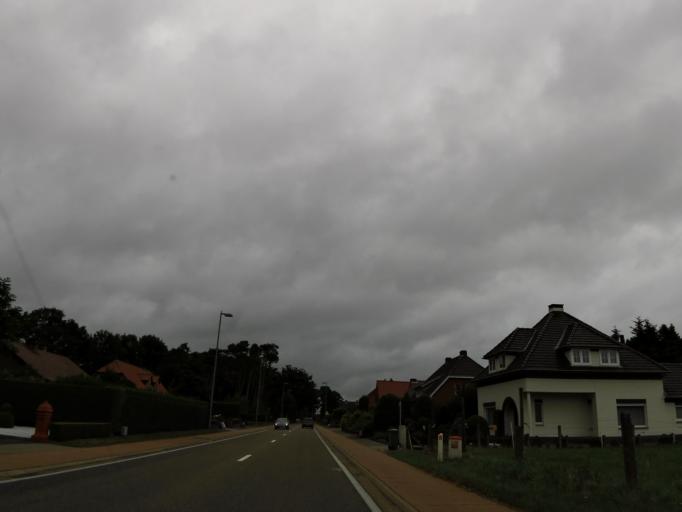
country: BE
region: Flanders
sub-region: Provincie Limburg
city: Bree
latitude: 51.0982
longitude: 5.5900
